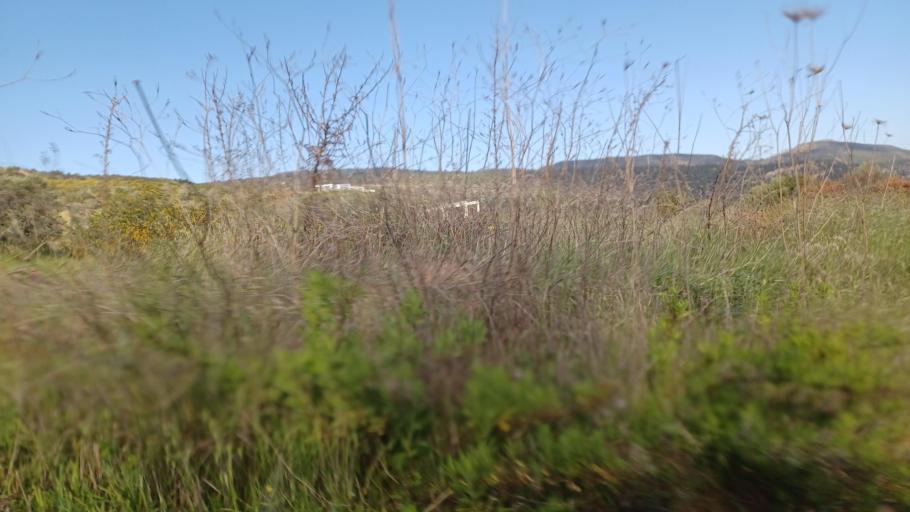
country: CY
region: Pafos
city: Polis
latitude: 35.0413
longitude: 32.3660
